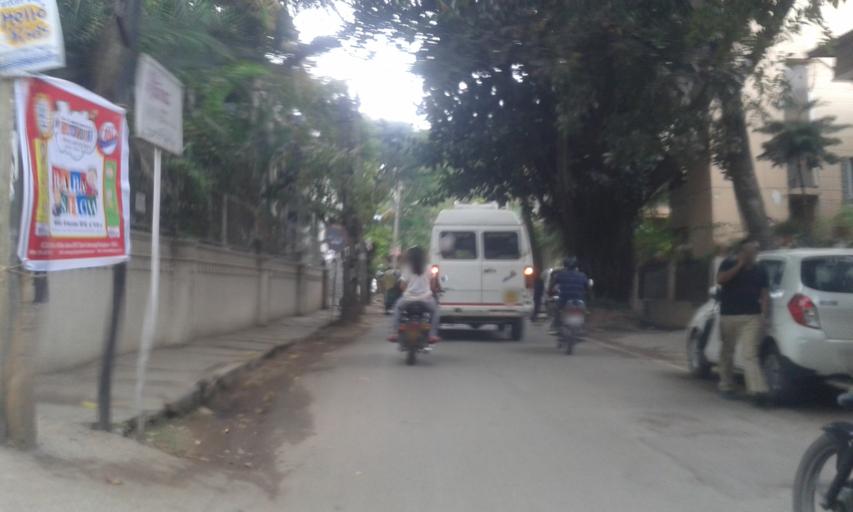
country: IN
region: Karnataka
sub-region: Bangalore Urban
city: Bangalore
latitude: 12.9682
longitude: 77.6462
